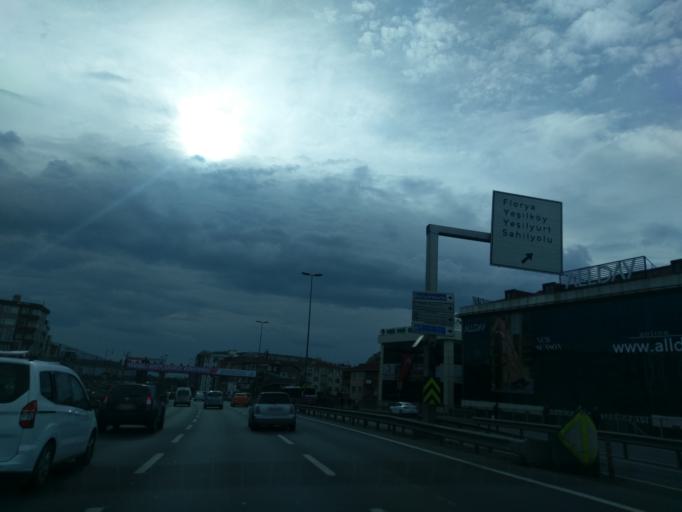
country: TR
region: Istanbul
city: Bahcelievler
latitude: 40.9961
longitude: 28.7955
